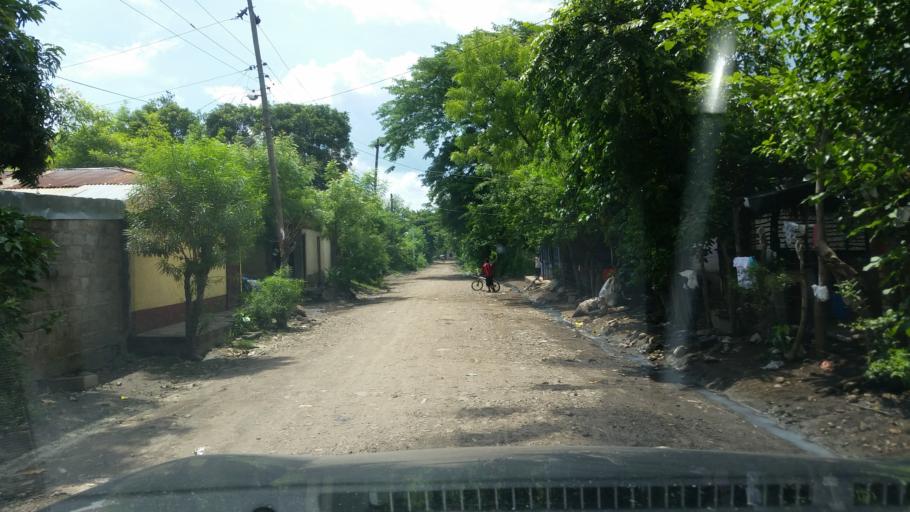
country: NI
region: Chinandega
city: Puerto Morazan
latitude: 12.7691
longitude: -87.1321
